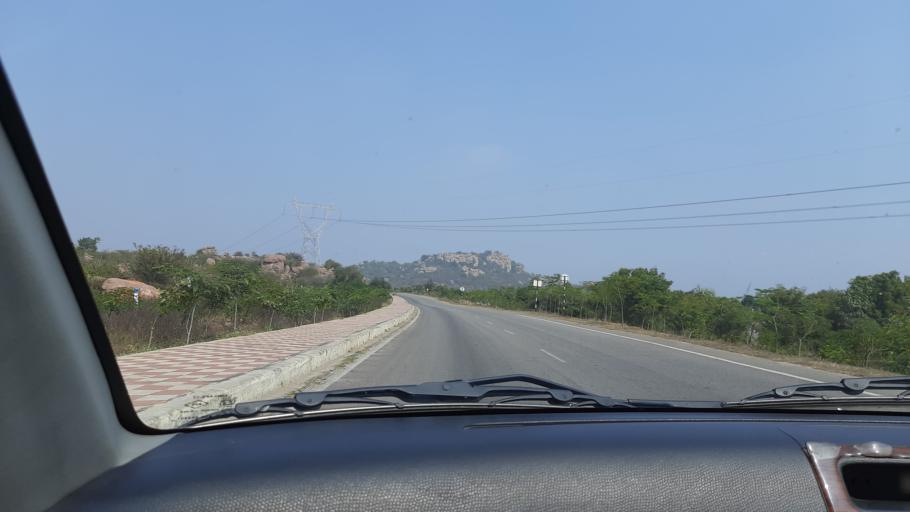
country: IN
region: Telangana
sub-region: Rangareddi
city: Lal Bahadur Nagar
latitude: 17.2826
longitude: 78.6484
